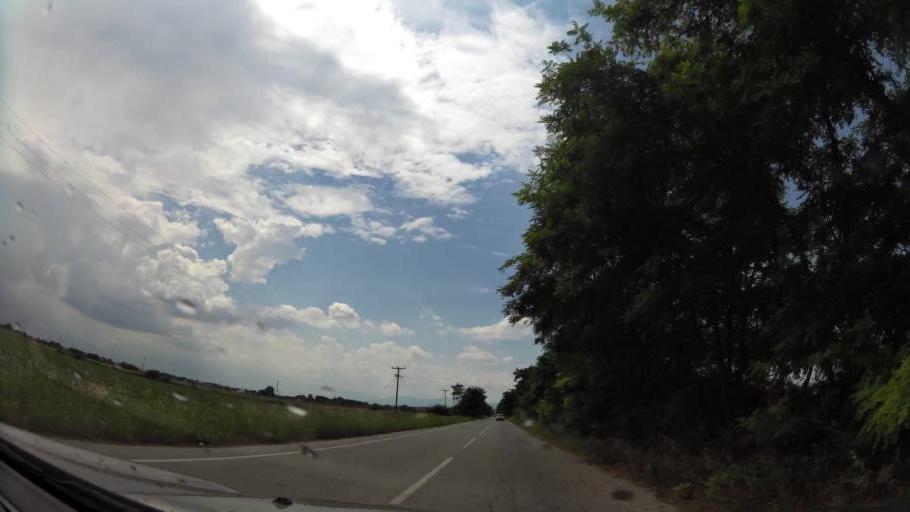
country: GR
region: Central Macedonia
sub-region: Nomos Pierias
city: Korinos
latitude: 40.3106
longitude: 22.6043
